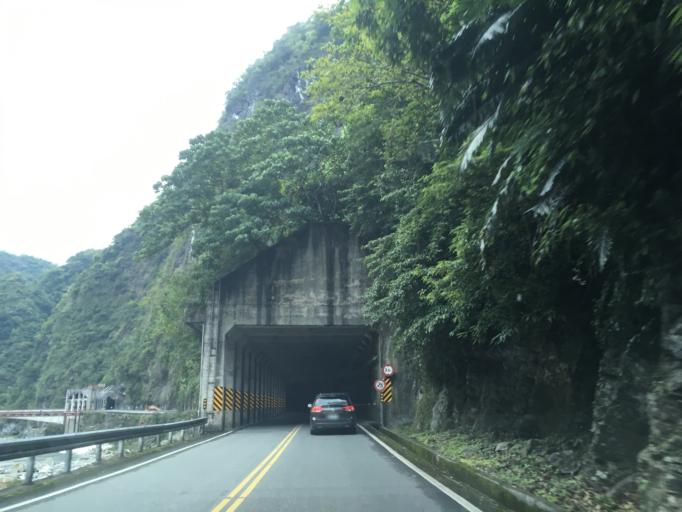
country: TW
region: Taiwan
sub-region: Hualien
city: Hualian
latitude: 24.1706
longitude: 121.6022
